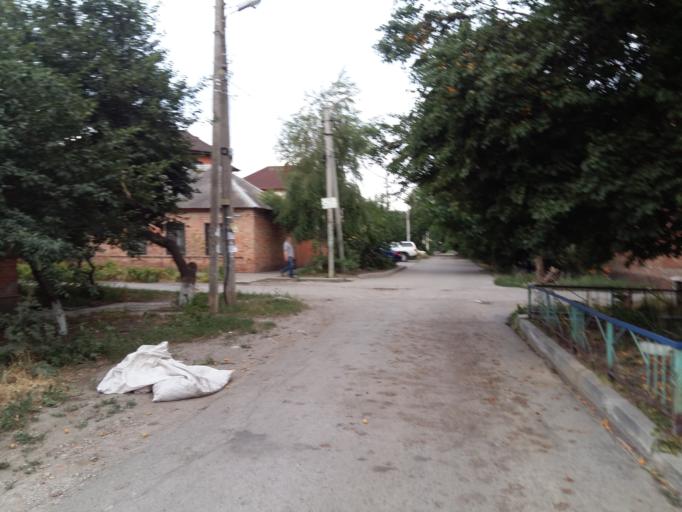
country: RU
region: Rostov
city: Imeni Chkalova
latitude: 47.2802
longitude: 39.7395
